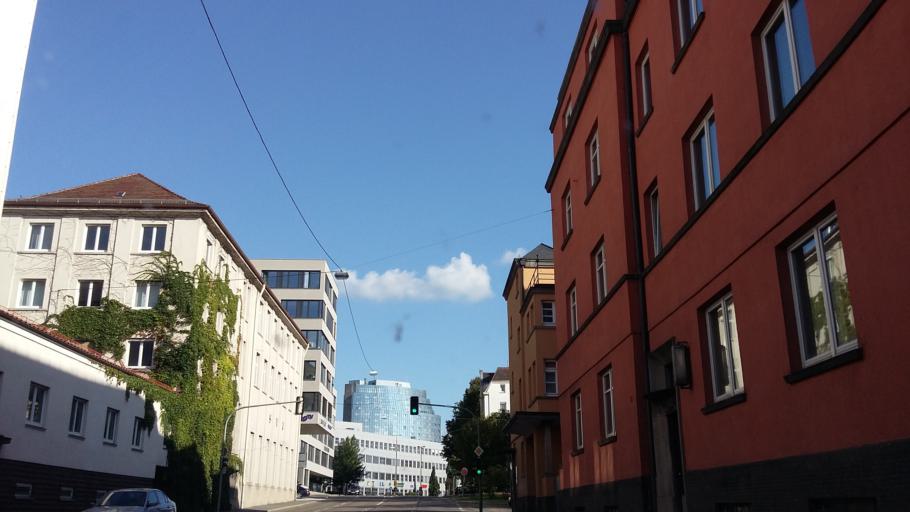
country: DE
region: Baden-Wuerttemberg
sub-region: Tuebingen Region
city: Ulm
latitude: 48.4022
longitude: 10.0001
